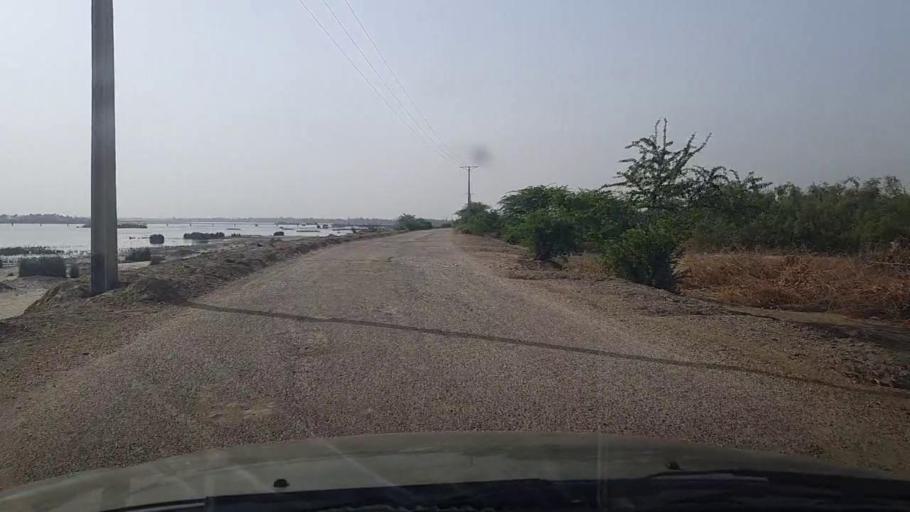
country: PK
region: Sindh
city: Kot Diji
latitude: 27.2953
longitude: 68.6435
